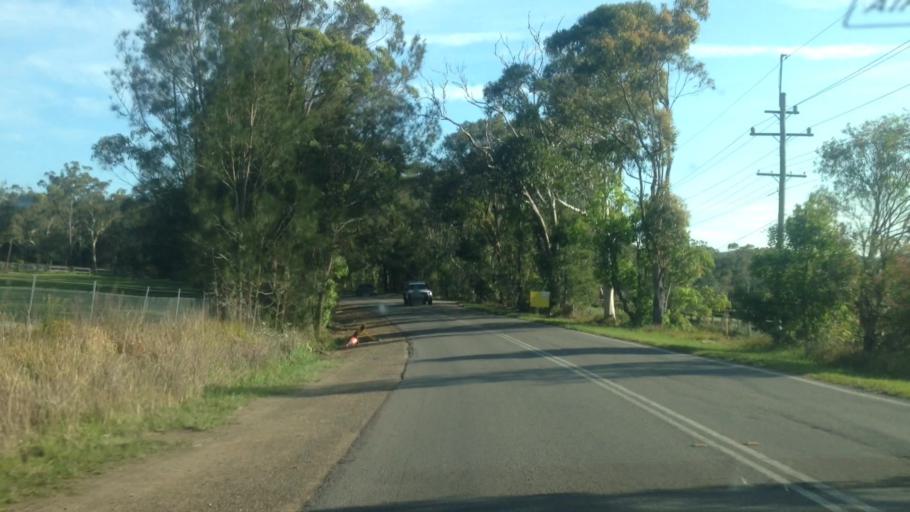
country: AU
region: New South Wales
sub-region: Lake Macquarie Shire
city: Dora Creek
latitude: -33.1068
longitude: 151.4767
